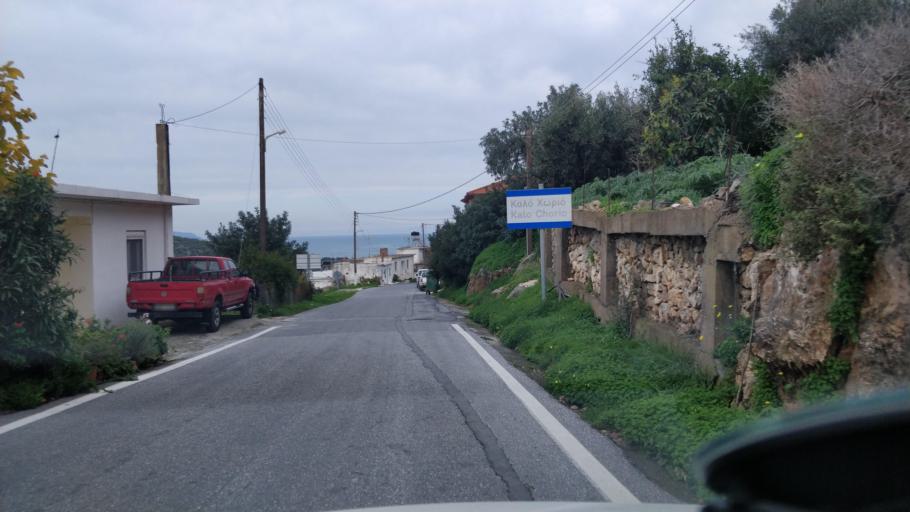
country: GR
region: Crete
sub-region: Nomos Lasithiou
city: Agios Nikolaos
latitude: 35.1137
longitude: 25.7216
